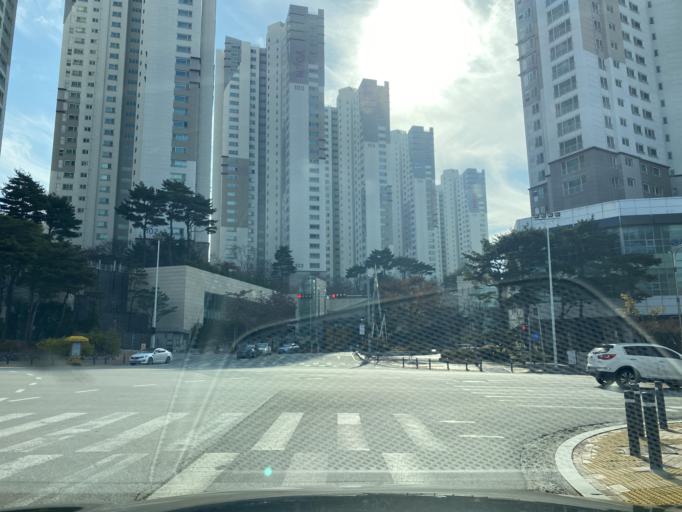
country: KR
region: Chungcheongnam-do
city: Cheonan
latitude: 36.7978
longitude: 127.1081
